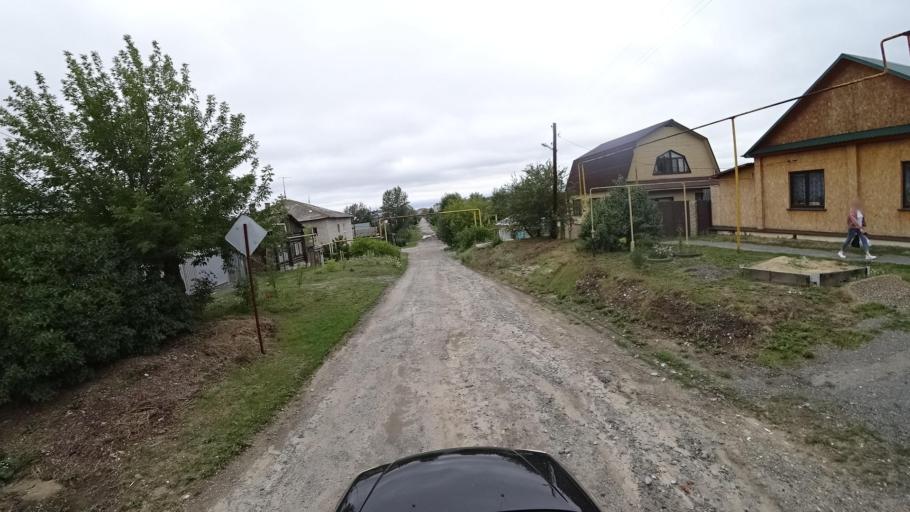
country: RU
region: Sverdlovsk
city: Kamyshlov
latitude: 56.8397
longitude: 62.7224
